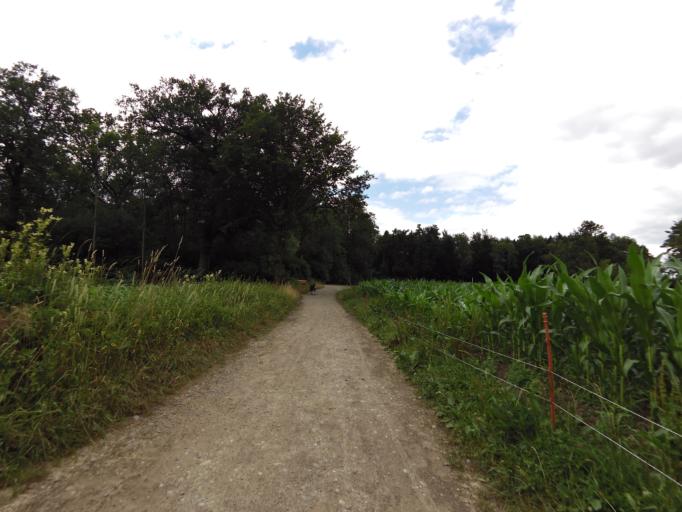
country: CH
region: Zurich
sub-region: Bezirk Zuerich
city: Zuerich (Kreis 10)
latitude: 47.4082
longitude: 8.5021
